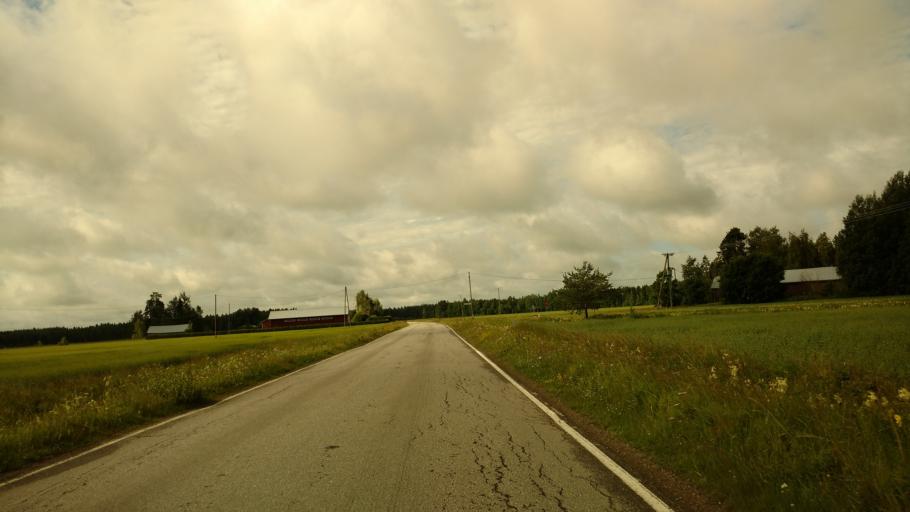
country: FI
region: Varsinais-Suomi
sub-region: Loimaa
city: Koski Tl
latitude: 60.7210
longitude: 23.1751
